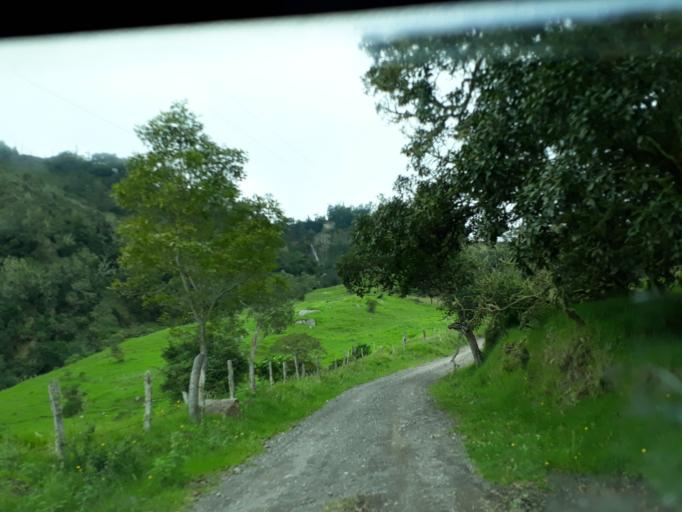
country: CO
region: Cundinamarca
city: Carmen de Carupa
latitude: 5.3769
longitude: -73.9773
